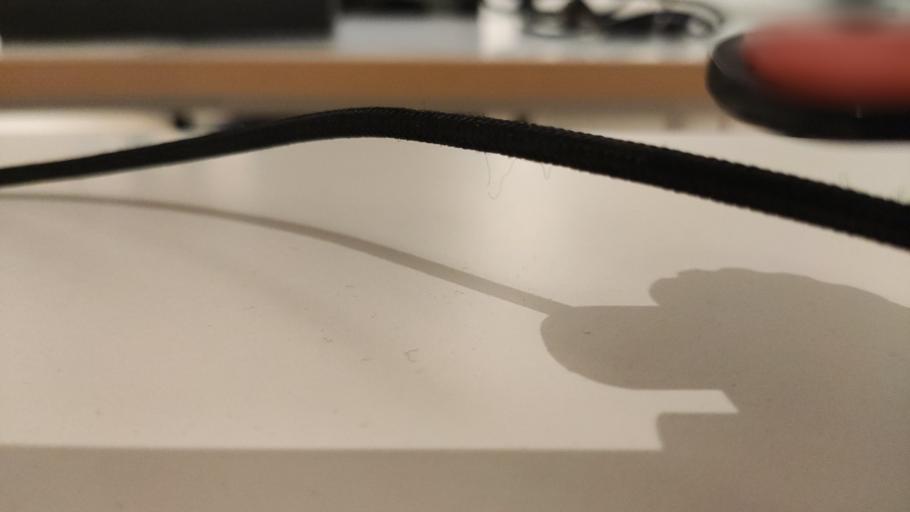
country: RU
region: Moskovskaya
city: Dorokhovo
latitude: 55.3993
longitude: 36.3830
